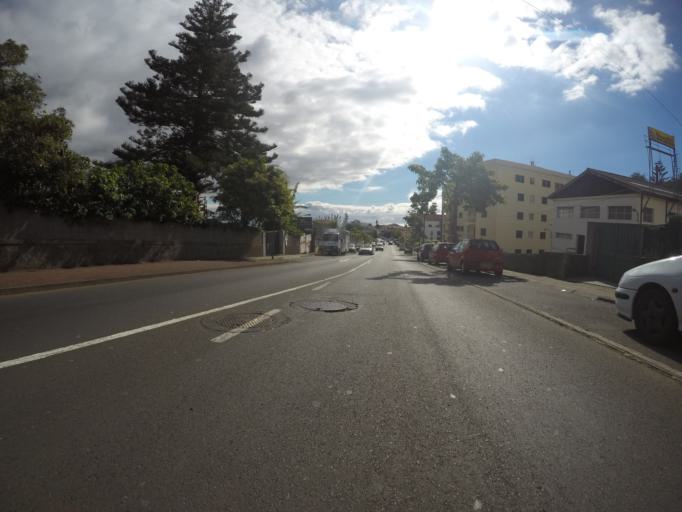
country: PT
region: Madeira
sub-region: Funchal
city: Nossa Senhora do Monte
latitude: 32.6638
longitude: -16.9354
